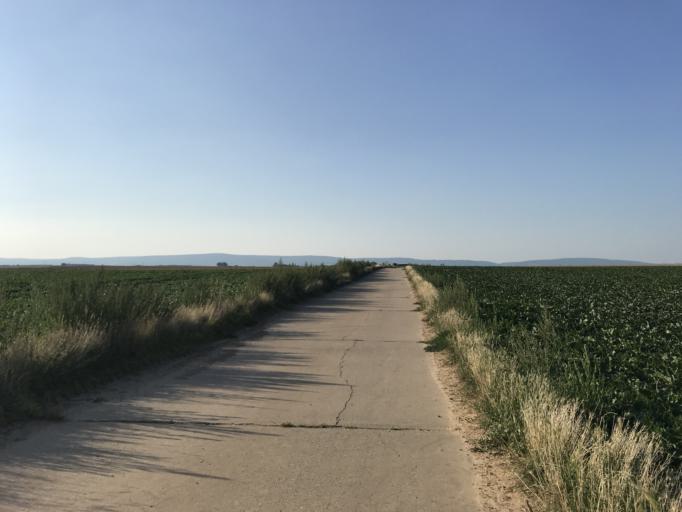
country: DE
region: Rheinland-Pfalz
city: Essenheim
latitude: 49.9367
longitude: 8.1528
